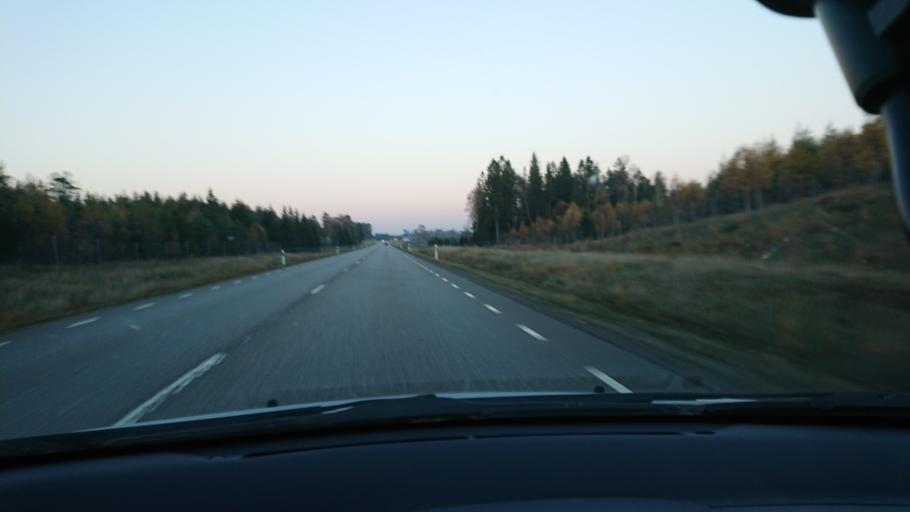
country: SE
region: Halland
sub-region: Laholms Kommun
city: Knared
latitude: 56.7444
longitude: 13.4844
